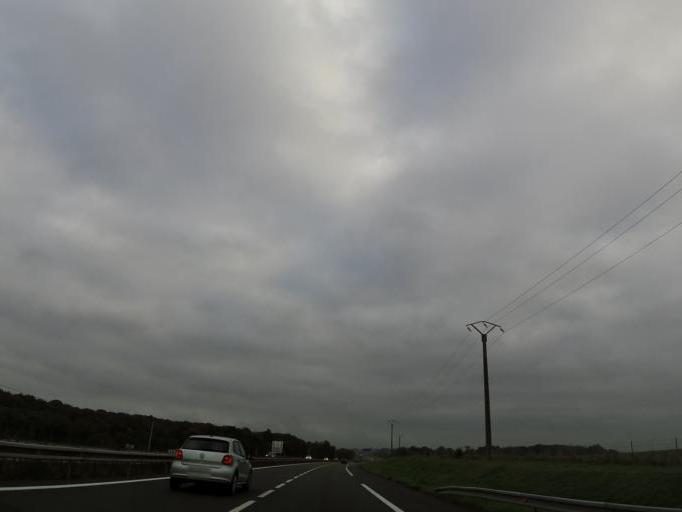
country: FR
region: Ile-de-France
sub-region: Departement de Seine-et-Marne
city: Sammeron
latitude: 48.9672
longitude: 3.0575
